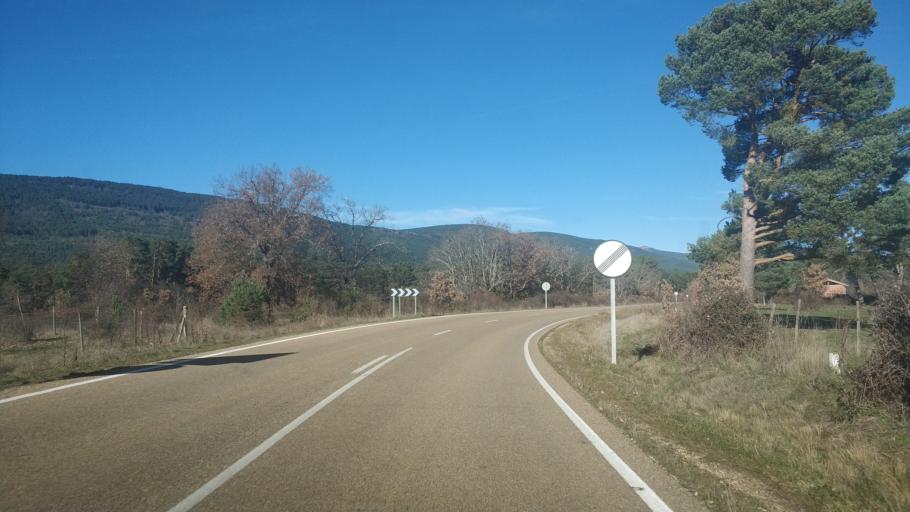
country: ES
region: Castille and Leon
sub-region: Provincia de Soria
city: Vinuesa
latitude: 41.9209
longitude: -2.7600
